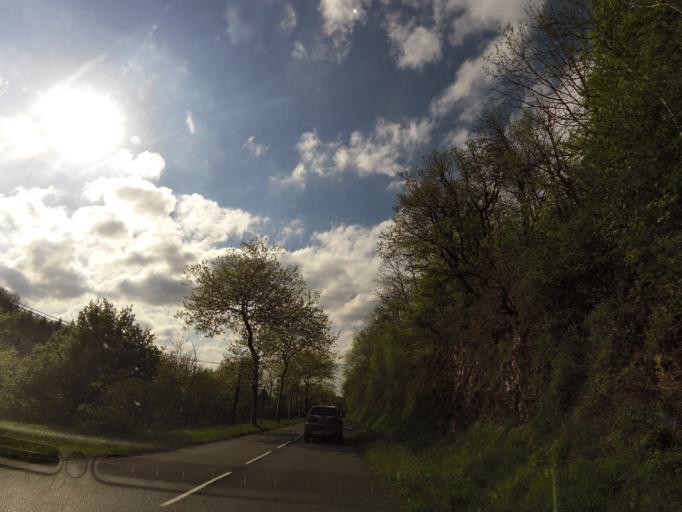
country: FR
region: Midi-Pyrenees
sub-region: Departement du Tarn
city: Soreze
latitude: 43.4315
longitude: 2.0525
